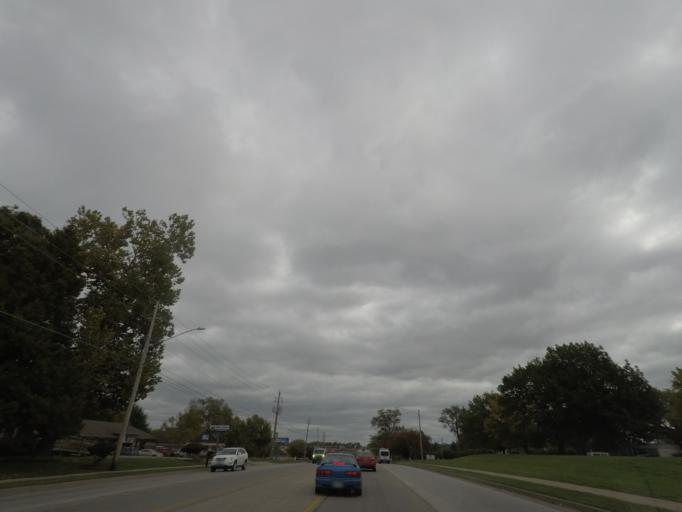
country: US
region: Iowa
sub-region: Polk County
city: Des Moines
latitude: 41.5263
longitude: -93.6089
